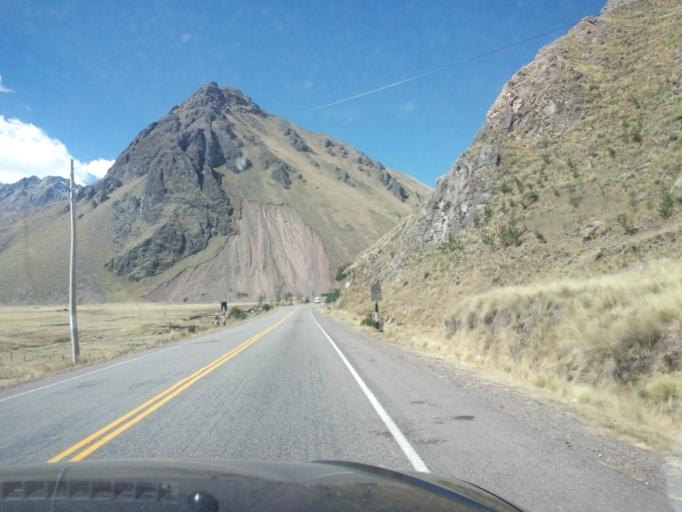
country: PE
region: Cusco
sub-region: Provincia de Canas
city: Layo
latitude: -14.4502
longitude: -71.0774
